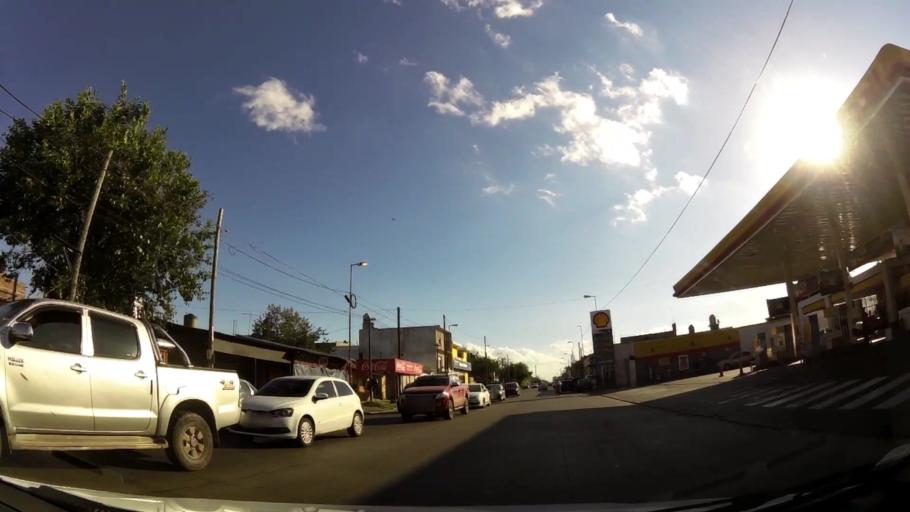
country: AR
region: Buenos Aires
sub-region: Partido de Moron
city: Moron
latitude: -34.6834
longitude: -58.6195
